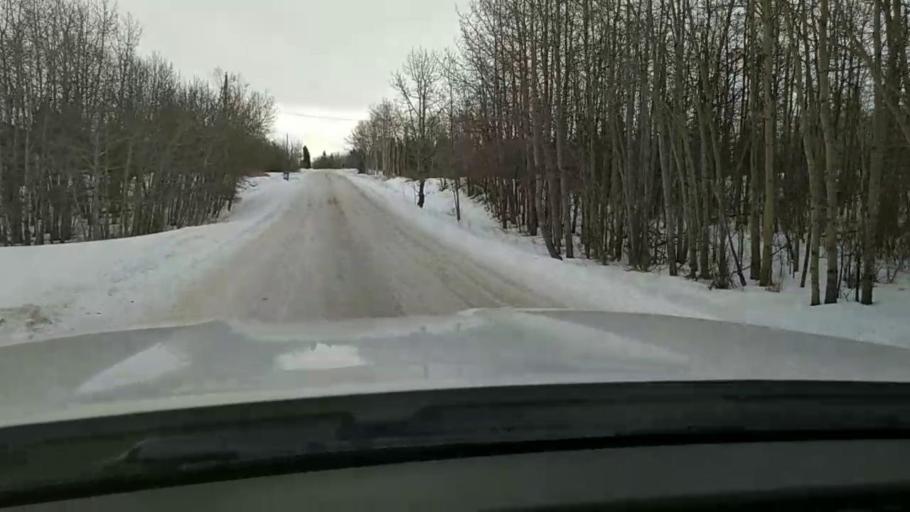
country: CA
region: Alberta
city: Cochrane
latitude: 51.1976
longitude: -114.2795
